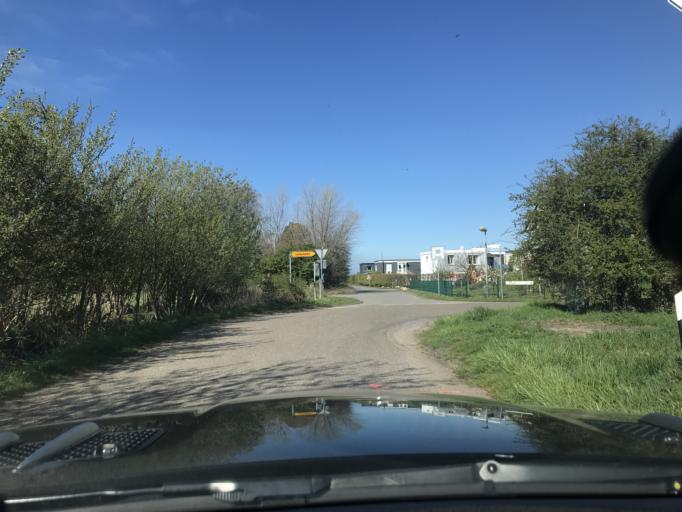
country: DE
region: Schleswig-Holstein
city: Grossenbrode
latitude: 54.4398
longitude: 11.0995
